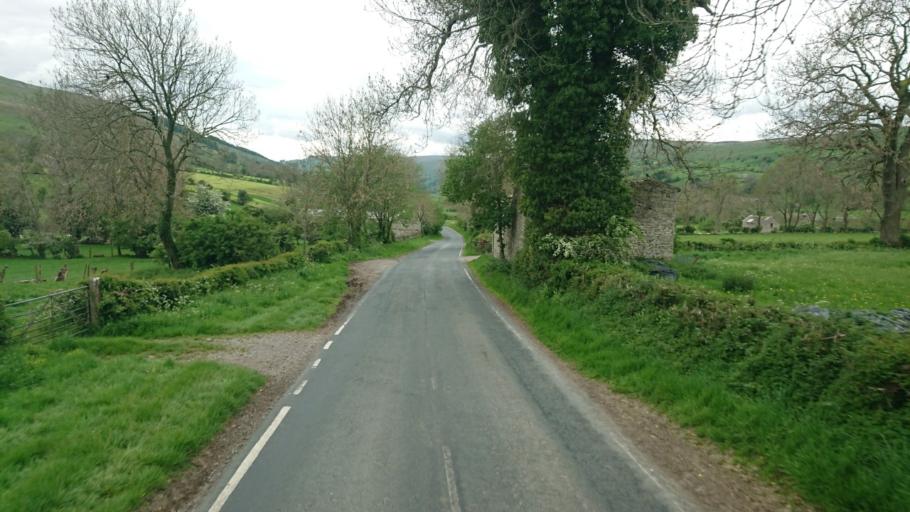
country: GB
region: England
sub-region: North Yorkshire
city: Leyburn
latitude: 54.2686
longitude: -2.0071
